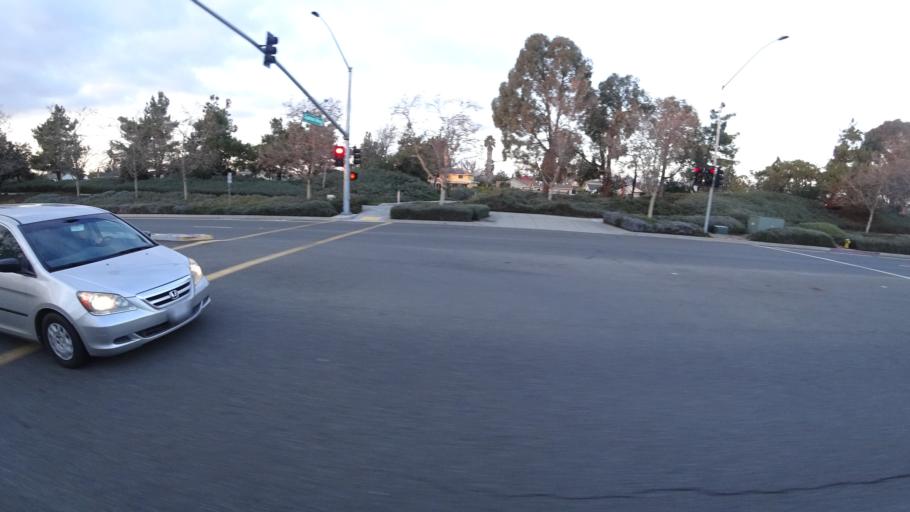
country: US
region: California
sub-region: Alameda County
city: Pleasanton
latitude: 37.6934
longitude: -121.8629
